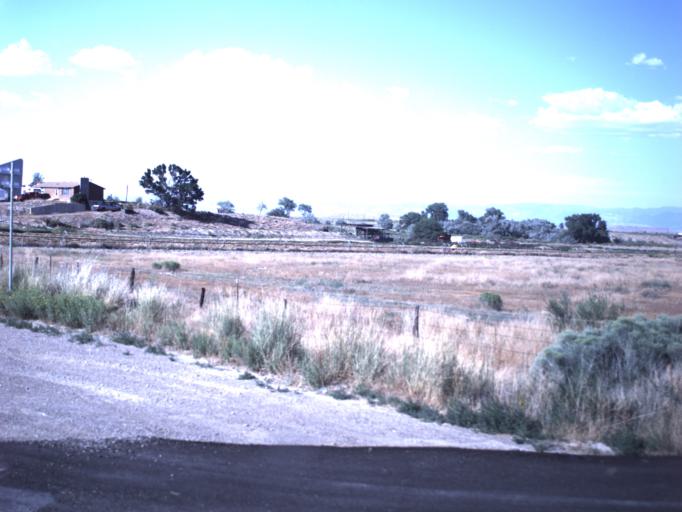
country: US
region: Utah
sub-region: Emery County
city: Huntington
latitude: 39.3930
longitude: -110.8525
